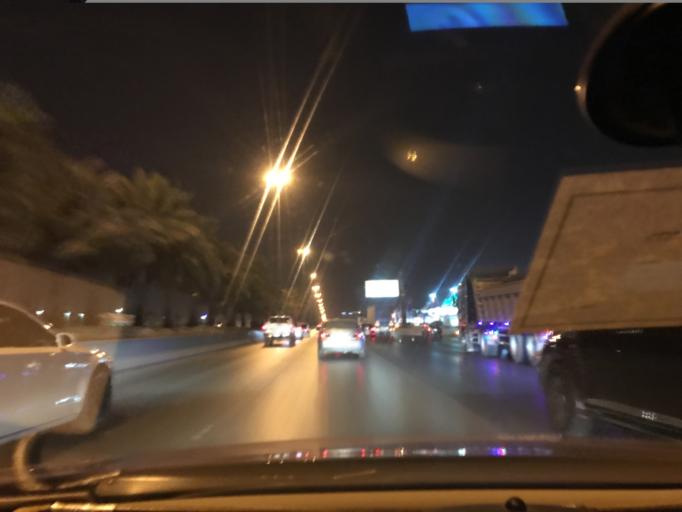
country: SA
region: Ar Riyad
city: Riyadh
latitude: 24.7619
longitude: 46.7379
